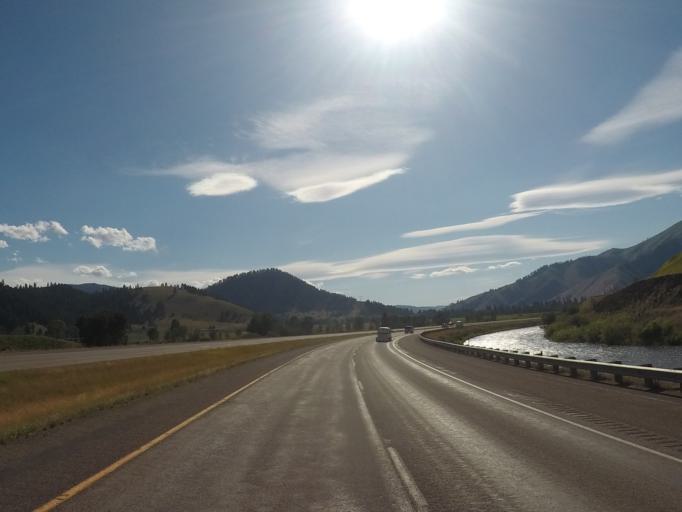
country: US
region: Montana
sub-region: Missoula County
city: Clinton
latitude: 46.6975
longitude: -113.3539
